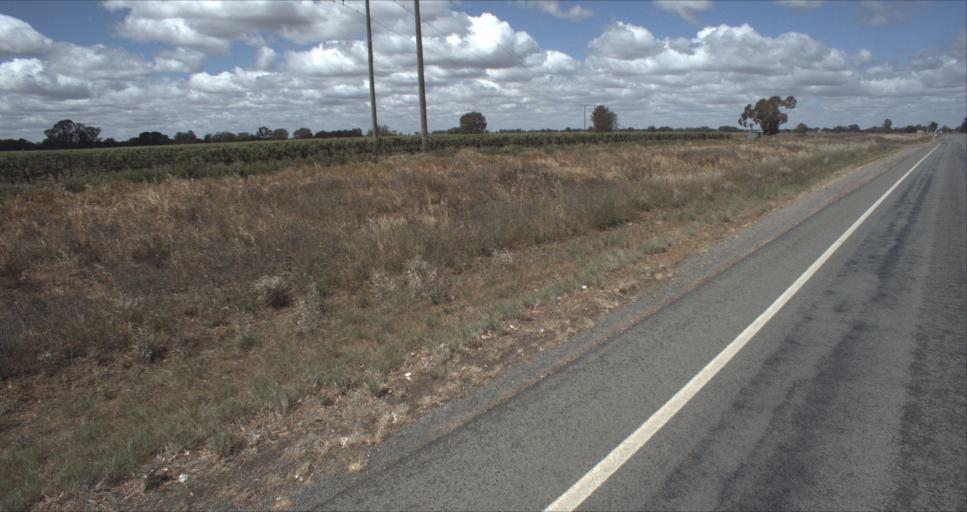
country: AU
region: New South Wales
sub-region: Murrumbidgee Shire
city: Darlington Point
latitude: -34.5068
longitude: 146.1871
